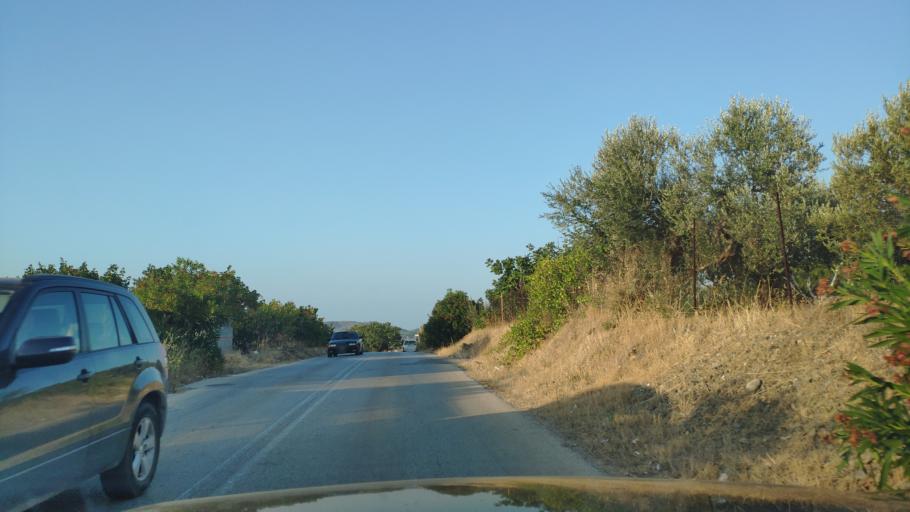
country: GR
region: Attica
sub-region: Nomarchia Anatolikis Attikis
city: Markopoulo
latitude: 37.8991
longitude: 23.9560
